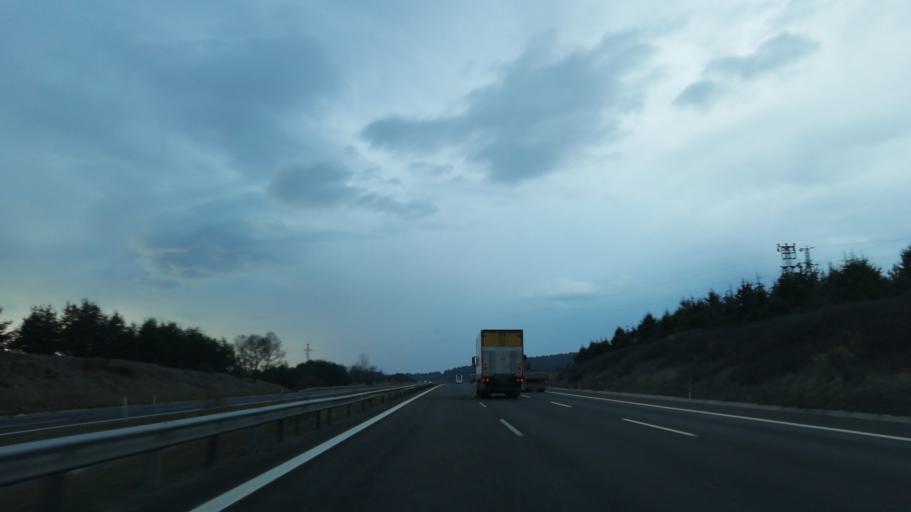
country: TR
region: Bolu
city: Yenicaga
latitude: 40.7520
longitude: 31.9280
